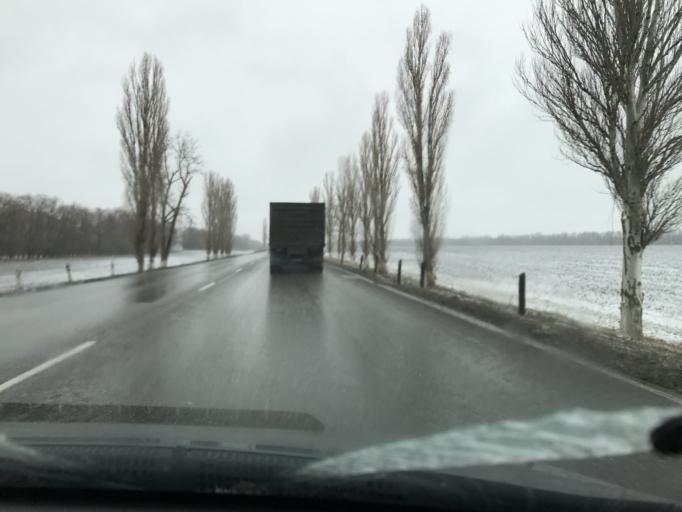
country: RU
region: Rostov
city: Kagal'nitskaya
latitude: 46.8426
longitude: 40.2182
